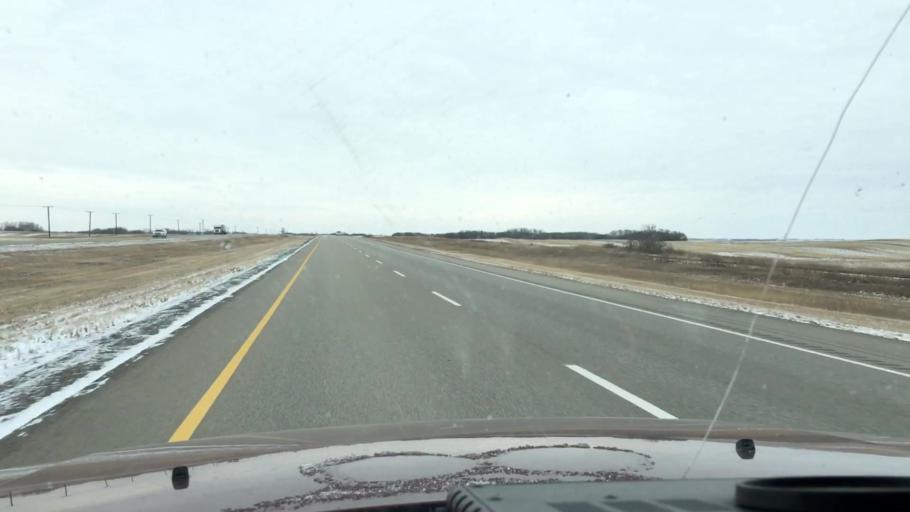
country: CA
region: Saskatchewan
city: Watrous
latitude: 51.3946
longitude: -106.1714
